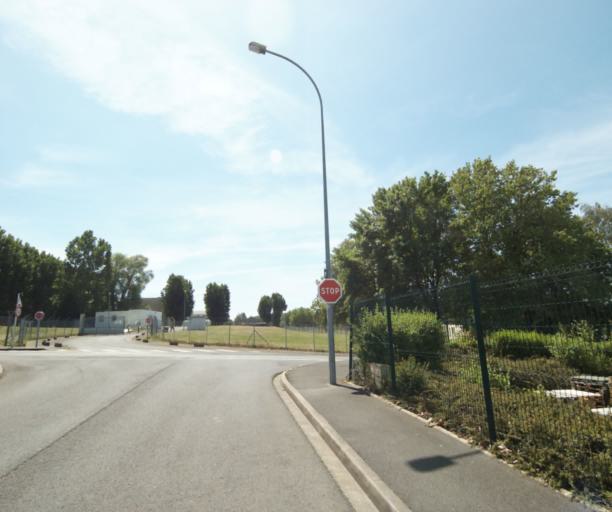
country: FR
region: Champagne-Ardenne
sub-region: Departement des Ardennes
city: Charleville-Mezieres
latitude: 49.7529
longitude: 4.7098
